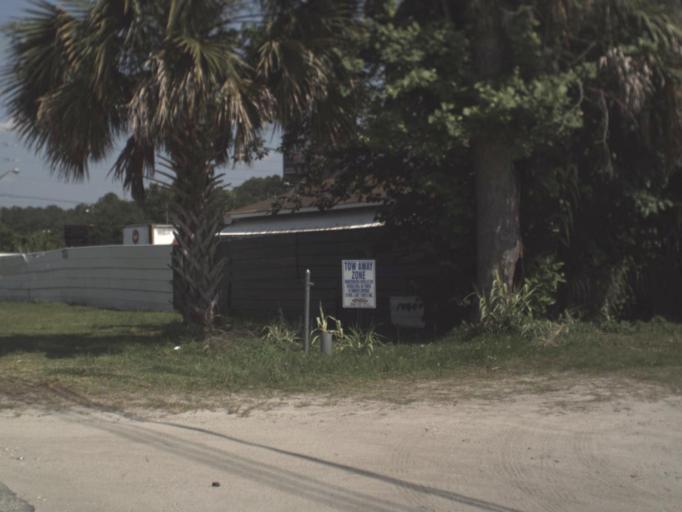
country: US
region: Florida
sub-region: Duval County
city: Jacksonville
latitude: 30.3617
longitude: -81.7306
